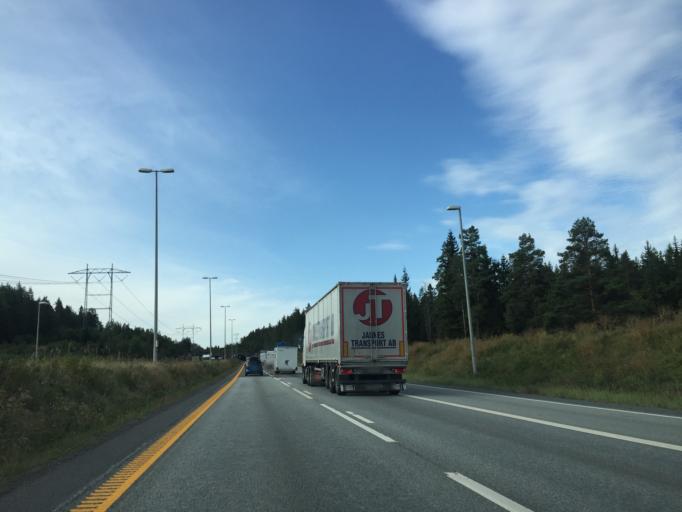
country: NO
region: Akershus
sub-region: Oppegard
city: Kolbotn
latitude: 59.7942
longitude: 10.8416
